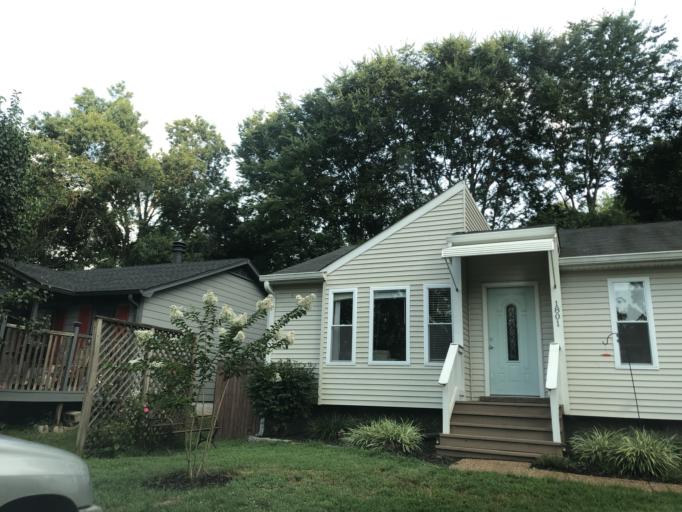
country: US
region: Tennessee
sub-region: Davidson County
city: Nashville
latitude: 36.1625
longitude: -86.7034
